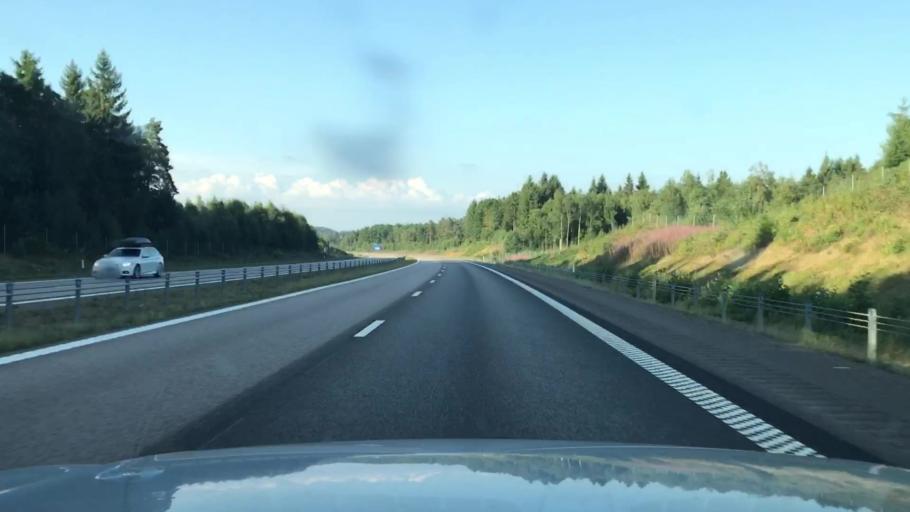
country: SE
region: Skane
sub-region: Orkelljunga Kommun
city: OErkelljunga
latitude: 56.2689
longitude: 13.3231
